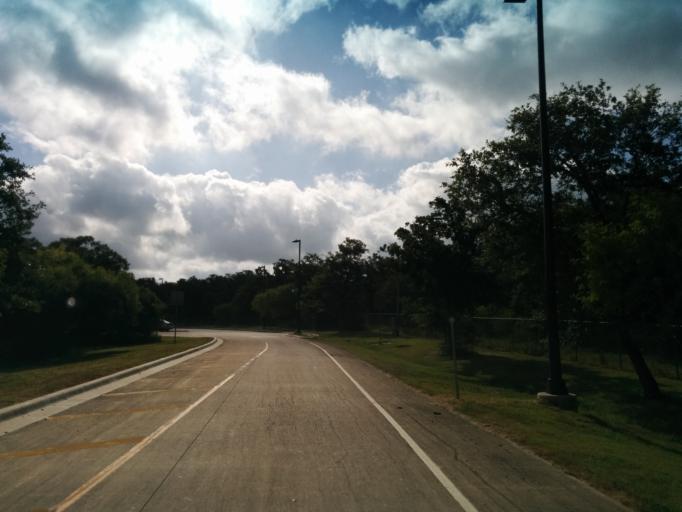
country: US
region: Texas
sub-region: Caldwell County
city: Luling
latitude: 29.6143
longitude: -97.8005
